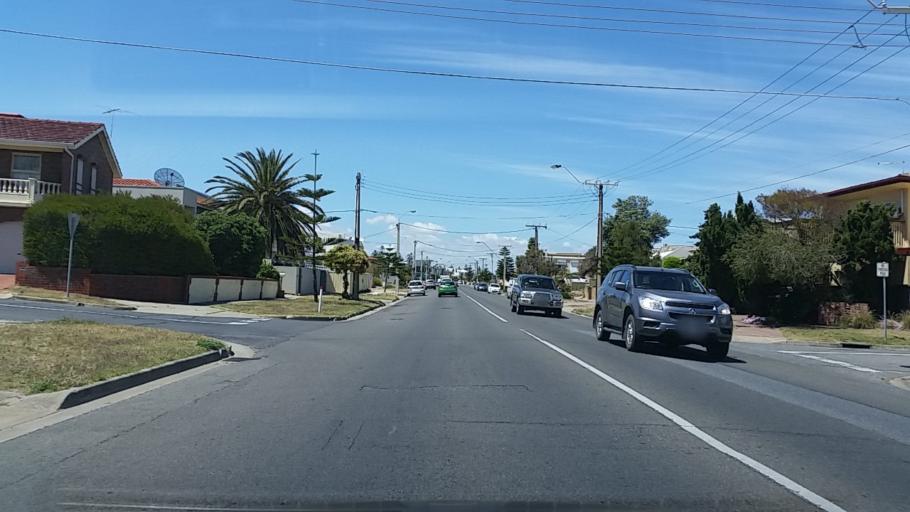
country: AU
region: South Australia
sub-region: Charles Sturt
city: Henley Beach
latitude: -34.9358
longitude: 138.4993
